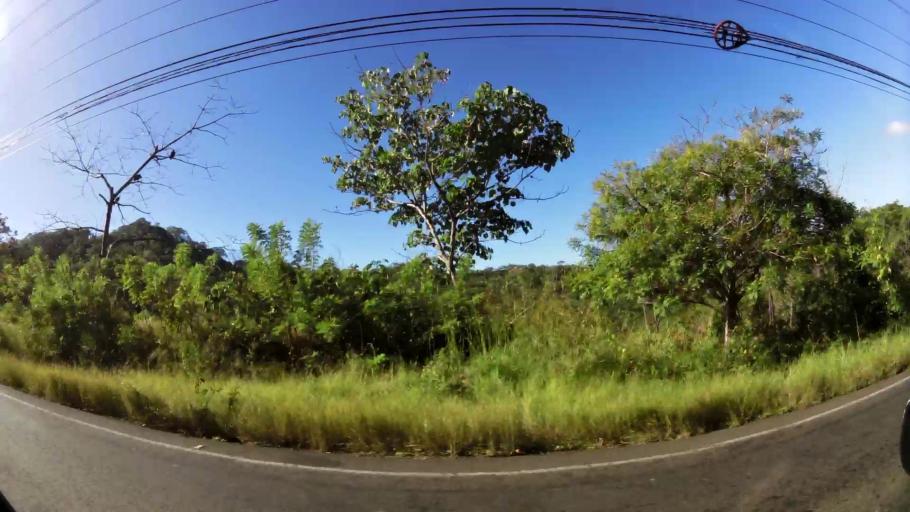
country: CR
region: Guanacaste
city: Belen
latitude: 10.3683
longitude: -85.7603
